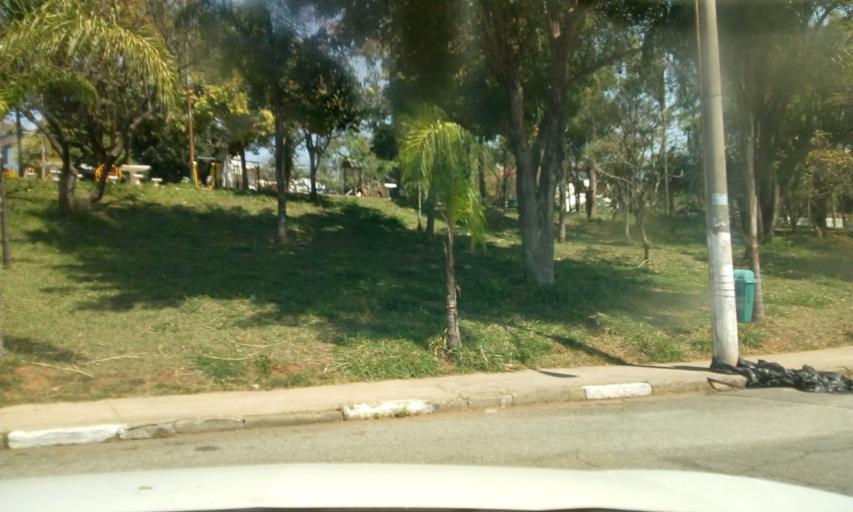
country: BR
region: Sao Paulo
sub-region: Osasco
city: Osasco
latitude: -23.5192
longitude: -46.7193
